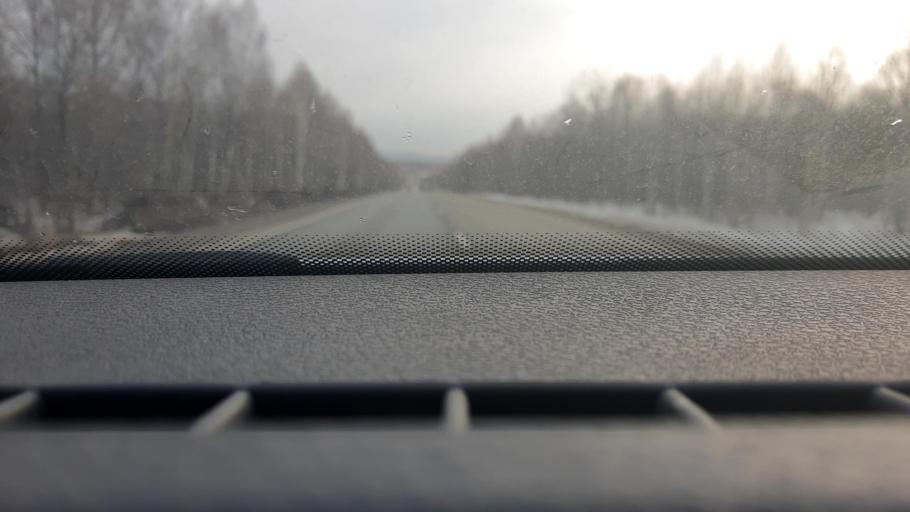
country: RU
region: Chelyabinsk
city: Asha
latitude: 54.8638
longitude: 57.1653
